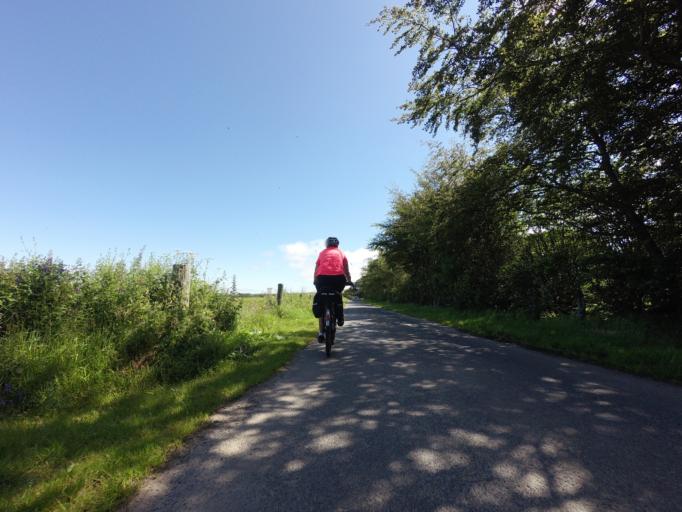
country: GB
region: Scotland
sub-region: Aberdeenshire
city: Macduff
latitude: 57.6281
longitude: -2.4877
